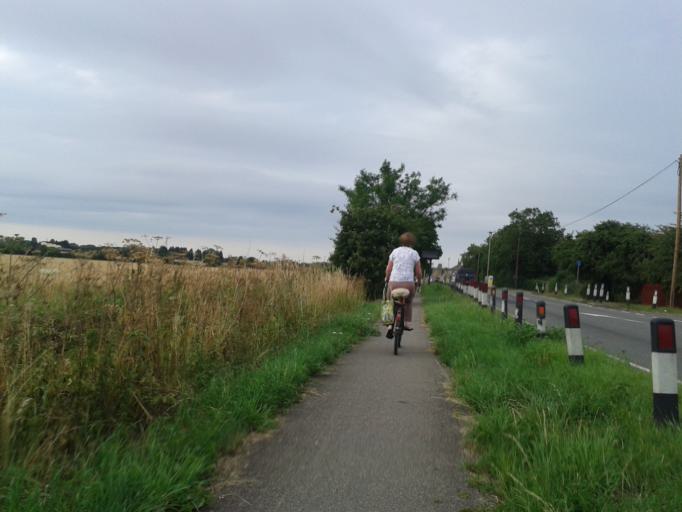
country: GB
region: England
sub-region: Cambridgeshire
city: Waterbeach
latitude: 52.2224
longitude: 0.1746
